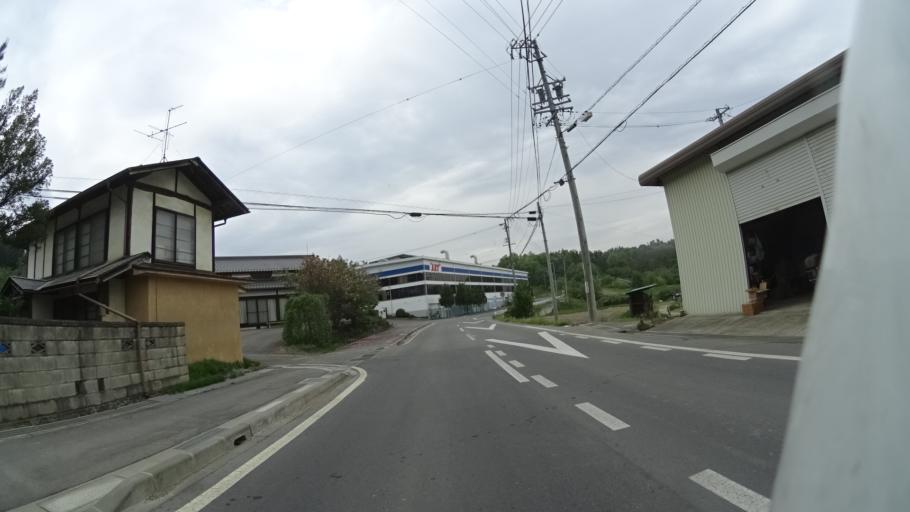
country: JP
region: Nagano
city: Kamimaruko
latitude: 36.3507
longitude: 138.1694
